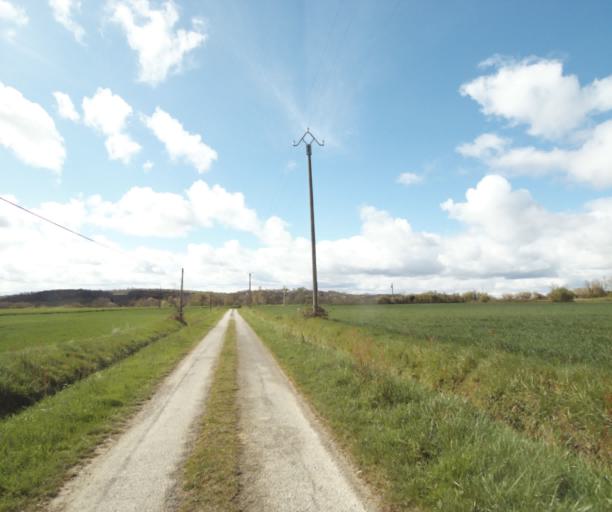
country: FR
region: Midi-Pyrenees
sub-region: Departement de l'Ariege
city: Saverdun
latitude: 43.2324
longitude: 1.5487
